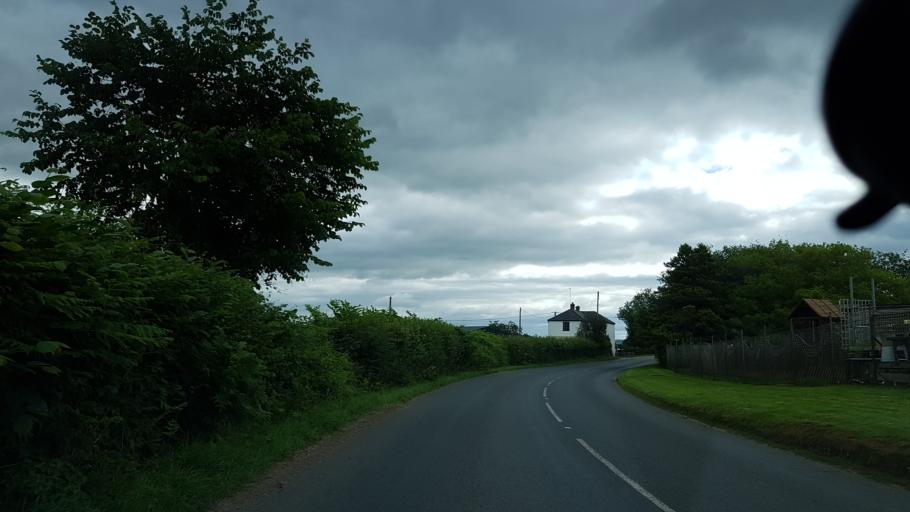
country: GB
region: Wales
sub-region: Monmouthshire
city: Llanarth
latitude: 51.7748
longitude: -2.8883
